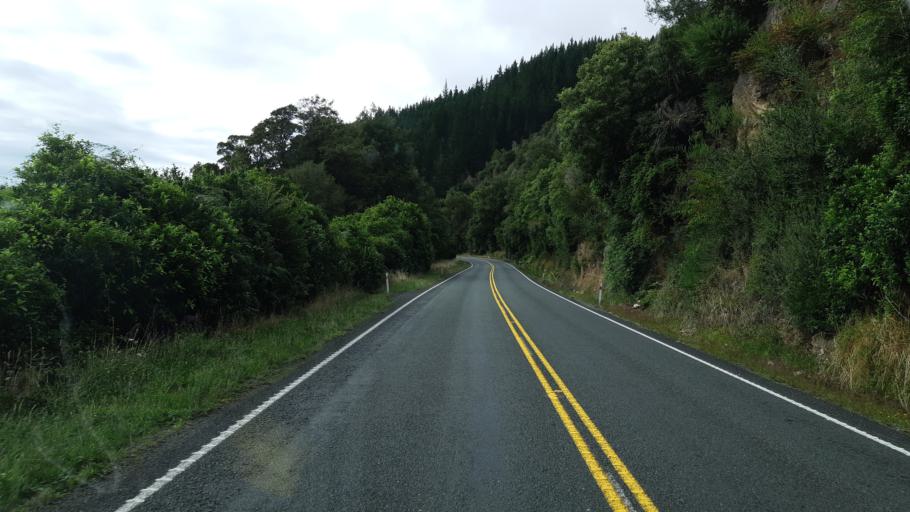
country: NZ
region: West Coast
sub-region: Buller District
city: Westport
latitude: -41.7772
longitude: 172.2455
